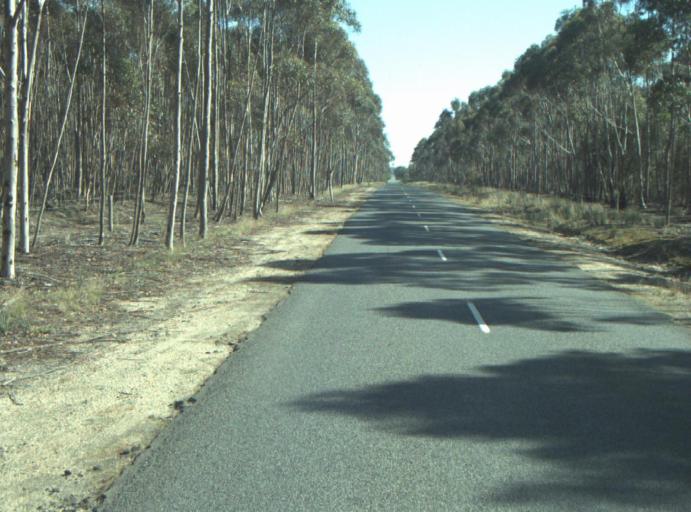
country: AU
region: Victoria
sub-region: Greater Geelong
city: Lara
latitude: -37.9436
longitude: 144.3921
